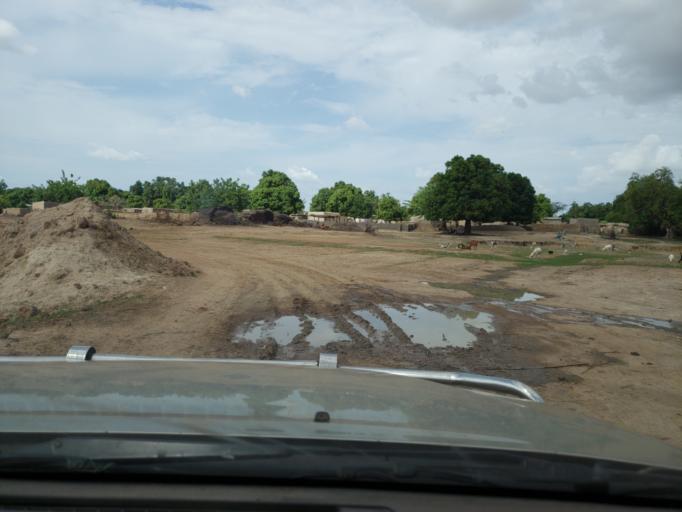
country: ML
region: Segou
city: Bla
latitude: 12.7309
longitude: -5.6707
